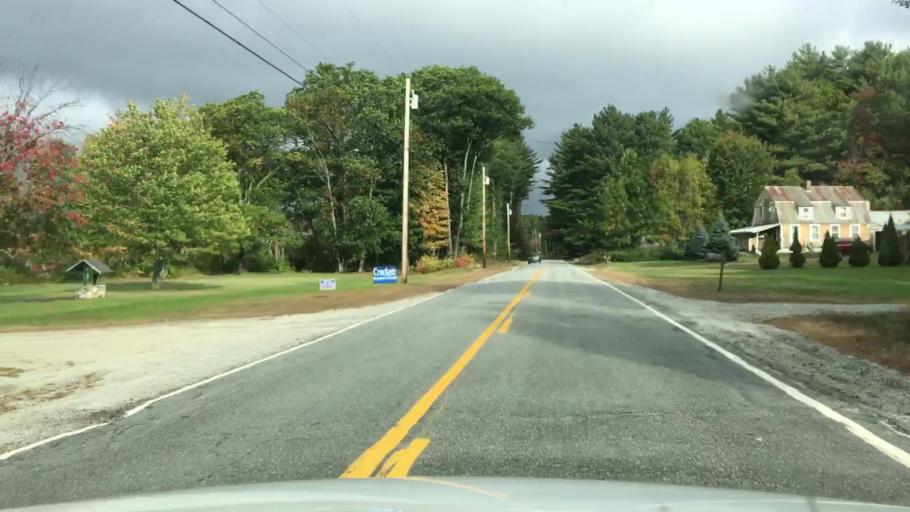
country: US
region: Maine
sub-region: Oxford County
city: Bethel
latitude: 44.3342
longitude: -70.7776
